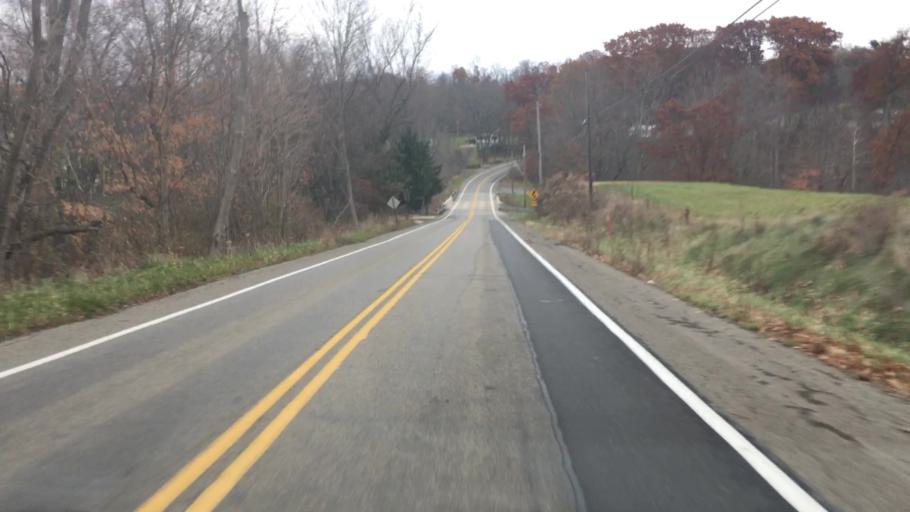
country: US
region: Pennsylvania
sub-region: Lawrence County
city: Bessemer
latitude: 40.9600
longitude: -80.4447
